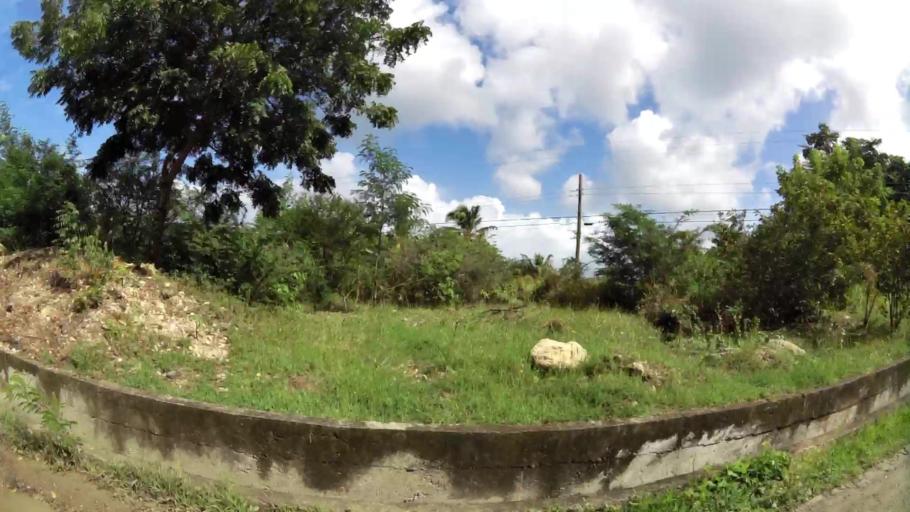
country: AG
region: Saint Mary
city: Bolands
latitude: 17.0695
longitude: -61.8742
